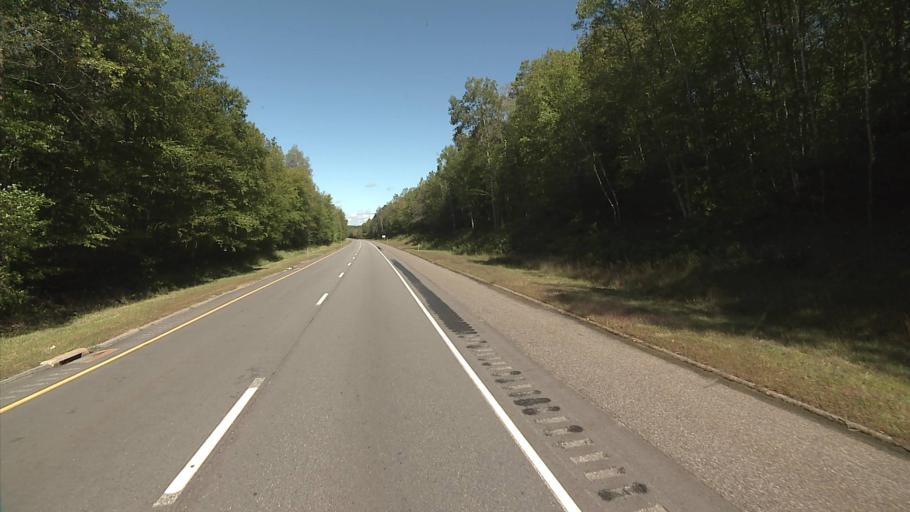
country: US
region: Connecticut
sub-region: New London County
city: Colchester
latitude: 41.5120
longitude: -72.3016
